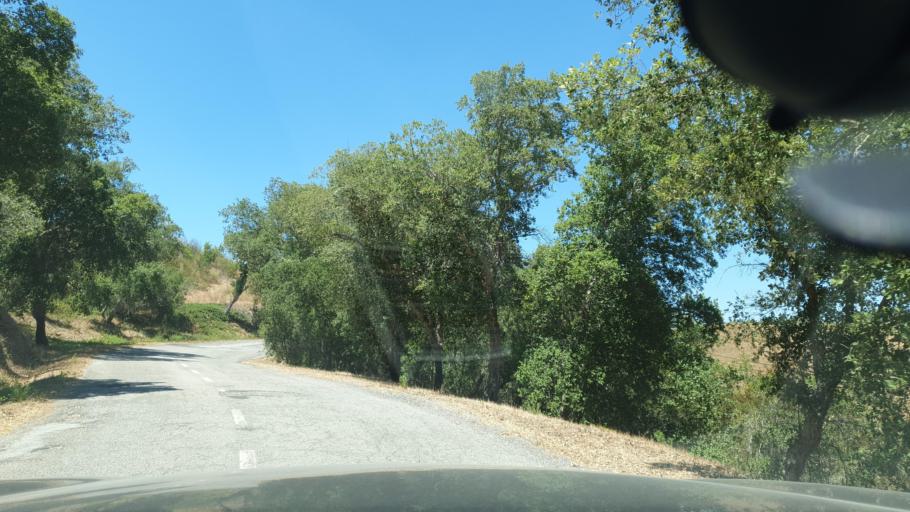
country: PT
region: Beja
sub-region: Odemira
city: Odemira
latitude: 37.6051
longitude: -8.4948
